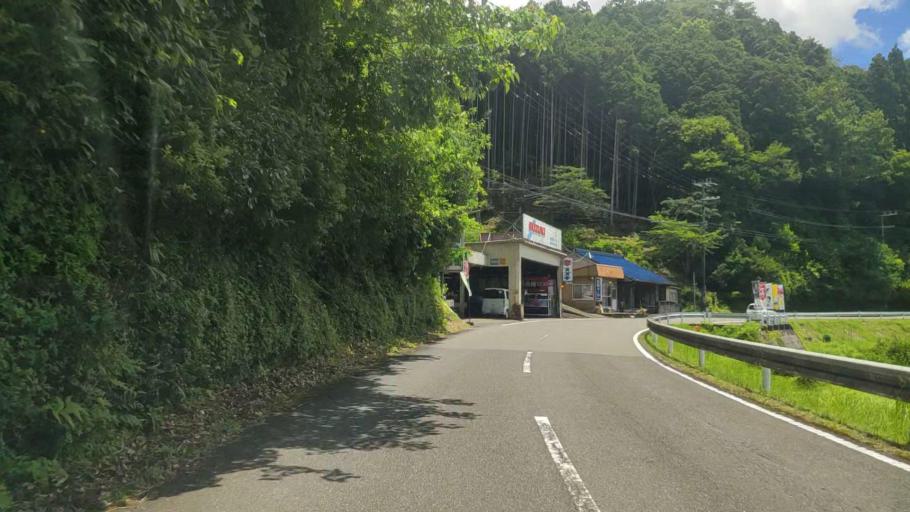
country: JP
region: Mie
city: Owase
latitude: 33.9623
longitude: 136.0657
